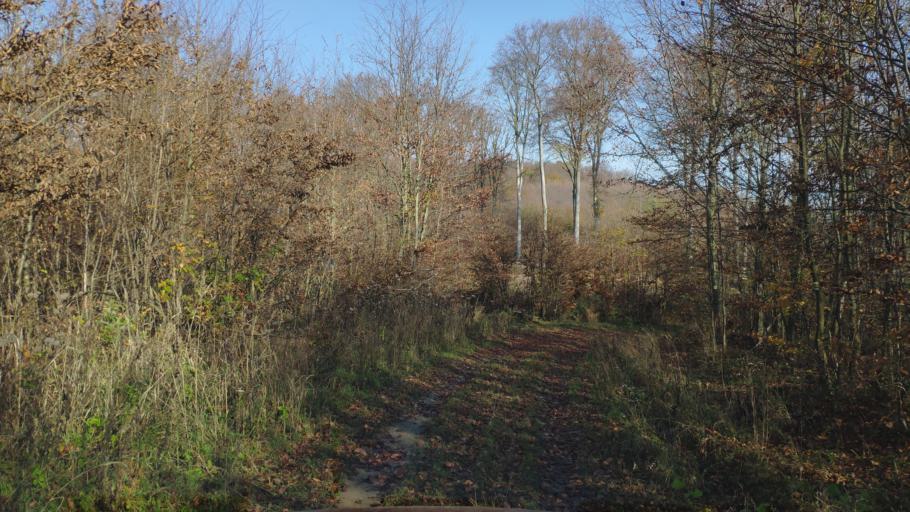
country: SK
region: Presovsky
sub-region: Okres Presov
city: Presov
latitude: 48.9012
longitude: 21.2150
